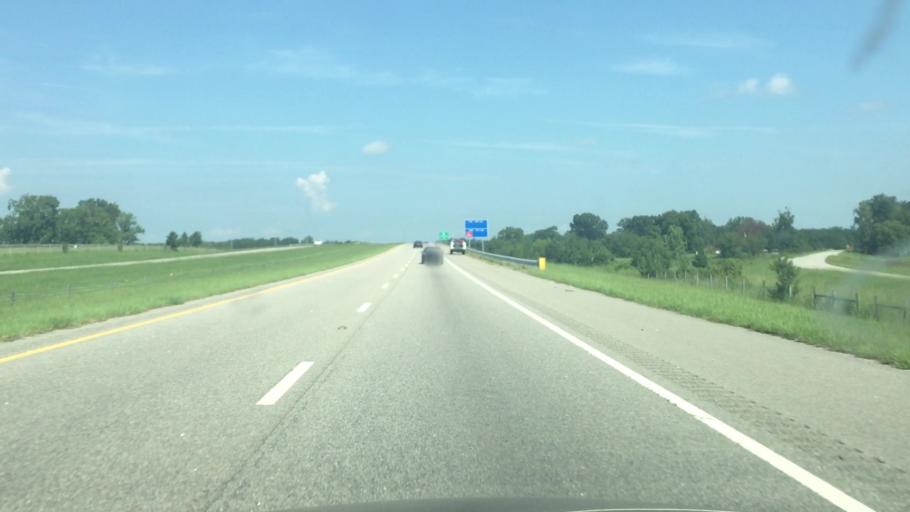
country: US
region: North Carolina
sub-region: Robeson County
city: Pembroke
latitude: 34.6466
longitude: -79.2408
